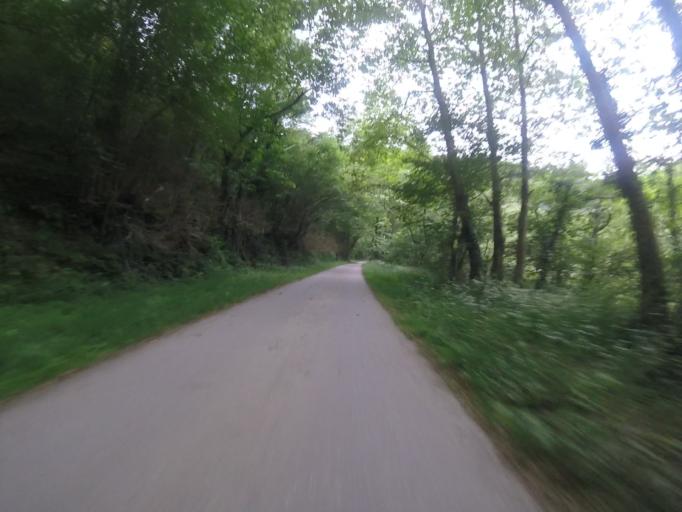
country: ES
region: Navarre
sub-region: Provincia de Navarra
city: Igantzi
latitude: 43.2172
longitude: -1.6763
